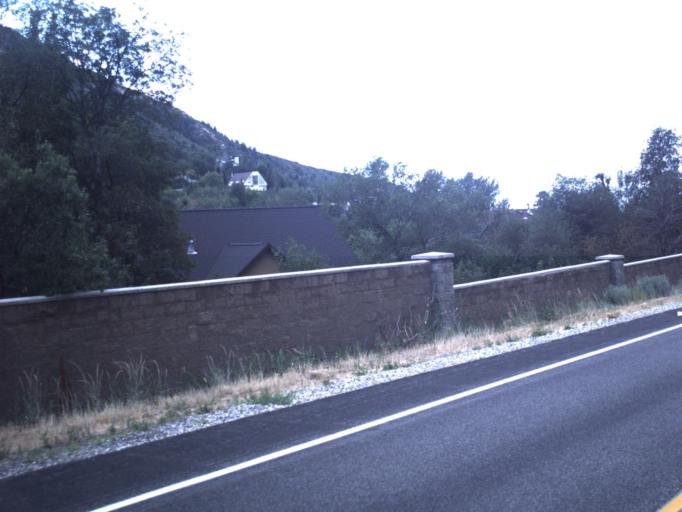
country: US
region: Utah
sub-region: Salt Lake County
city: Granite
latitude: 40.5742
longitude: -111.7800
